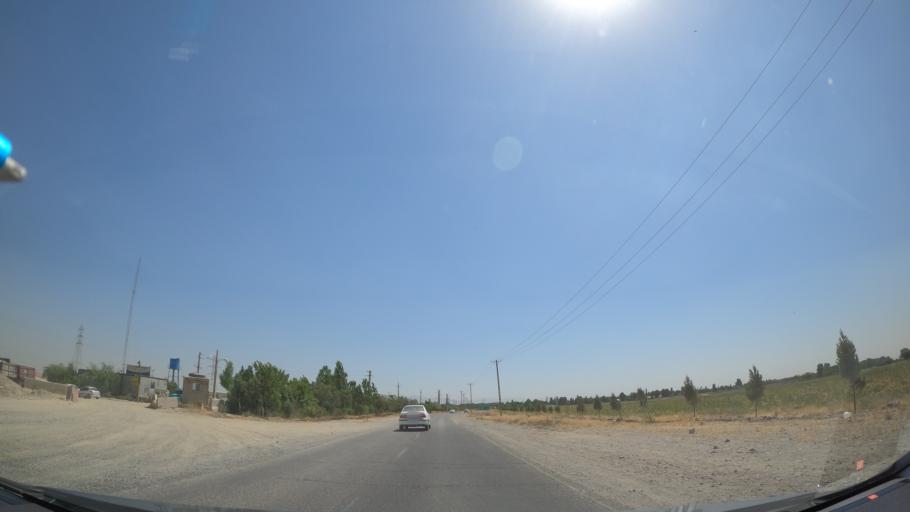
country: IR
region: Alborz
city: Hashtgerd
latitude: 35.9193
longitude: 50.7380
